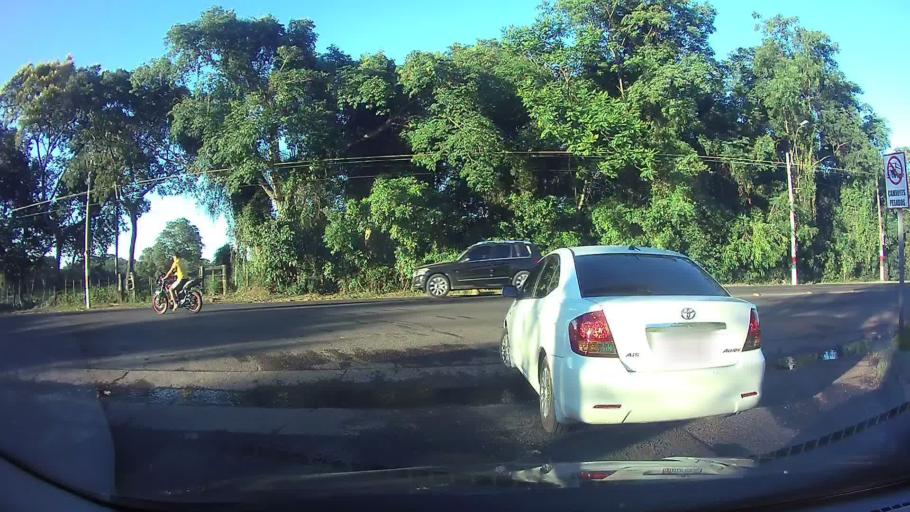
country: PY
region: Central
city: Aregua
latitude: -25.3051
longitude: -57.3953
